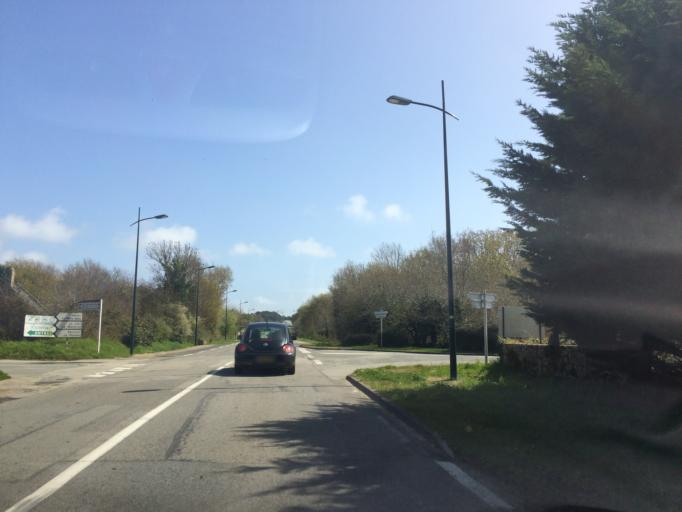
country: FR
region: Brittany
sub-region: Departement du Morbihan
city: La Trinite-sur-Mer
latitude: 47.5971
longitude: -3.0395
